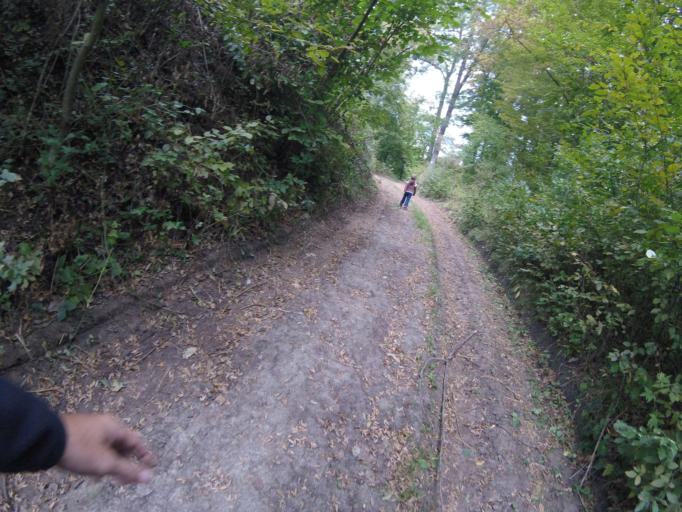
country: HU
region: Pest
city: Nagymaros
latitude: 47.8319
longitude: 18.9343
